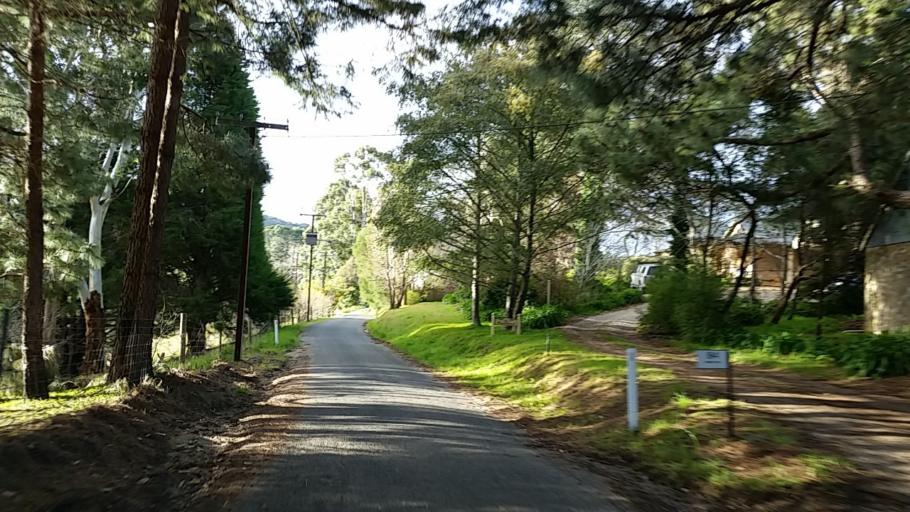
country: AU
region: South Australia
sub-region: Adelaide Hills
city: Adelaide Hills
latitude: -34.9350
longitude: 138.7680
